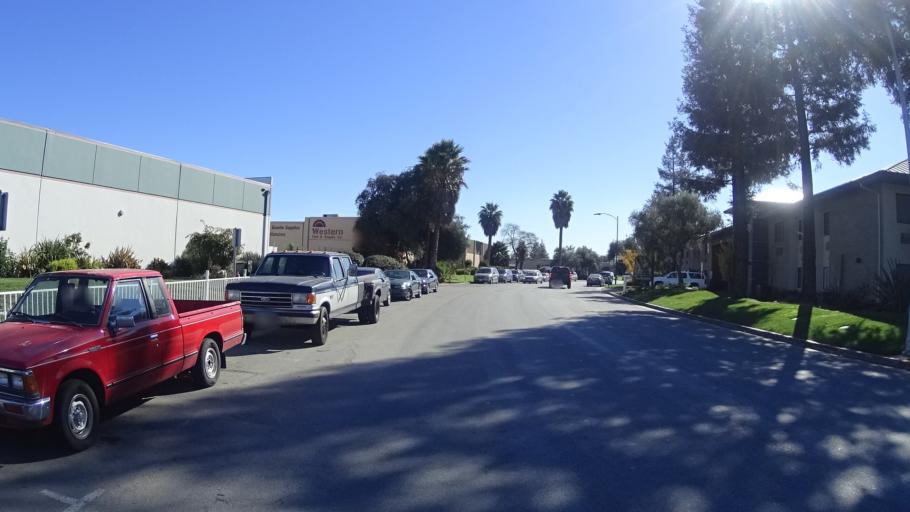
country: US
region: California
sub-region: Santa Clara County
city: Santa Clara
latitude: 37.3789
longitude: -121.9386
